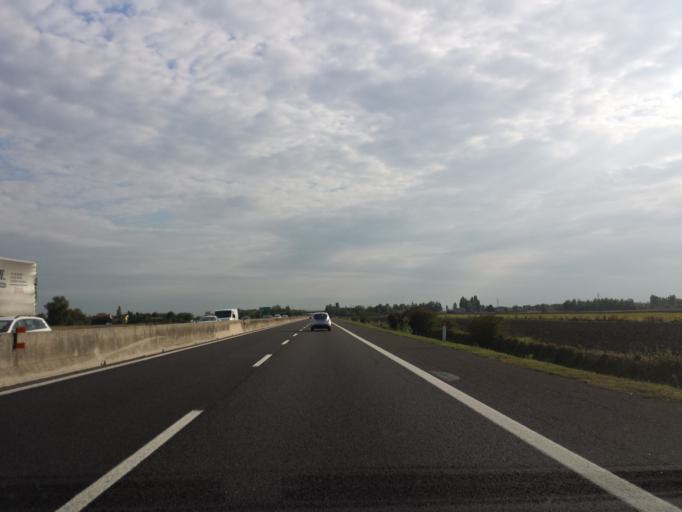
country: IT
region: Veneto
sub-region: Provincia di Padova
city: Solesino
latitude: 45.1632
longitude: 11.7757
